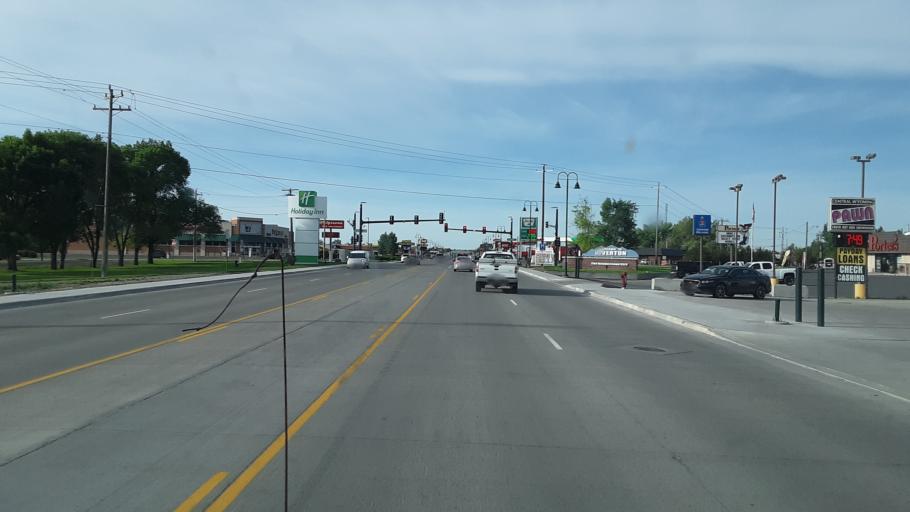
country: US
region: Wyoming
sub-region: Fremont County
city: Riverton
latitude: 43.0352
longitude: -108.3807
